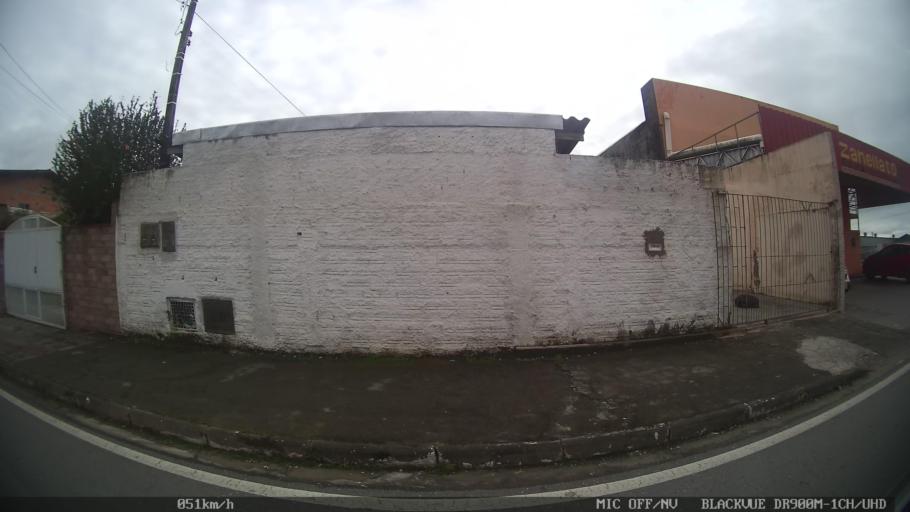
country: BR
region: Santa Catarina
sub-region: Biguacu
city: Biguacu
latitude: -27.5432
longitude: -48.6381
